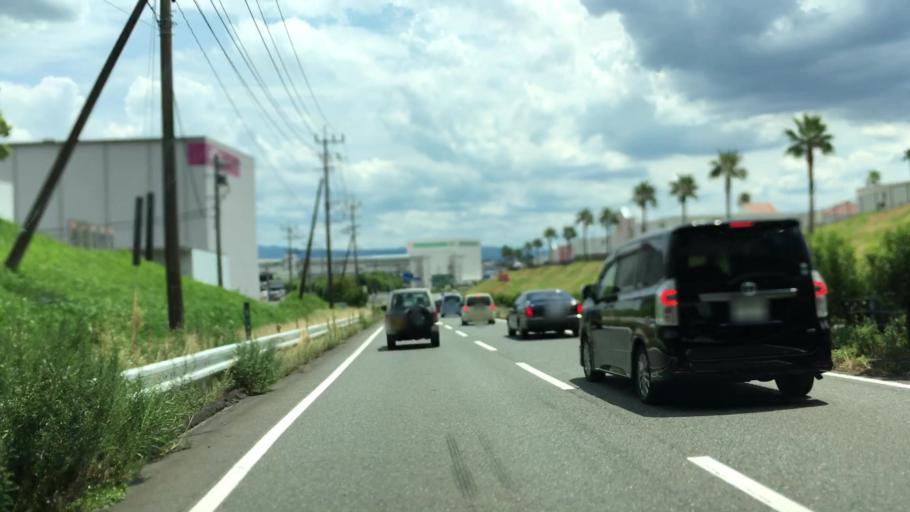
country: JP
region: Saga Prefecture
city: Tosu
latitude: 33.4089
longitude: 130.5116
